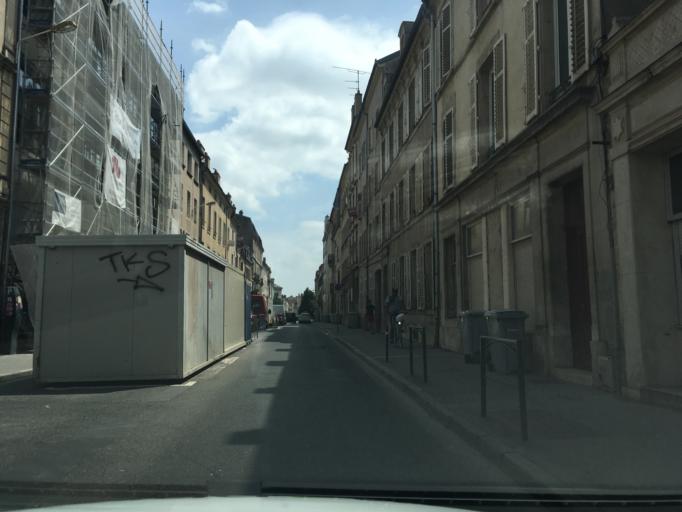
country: FR
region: Lorraine
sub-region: Departement de Meurthe-et-Moselle
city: Nancy
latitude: 48.6868
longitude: 6.1896
